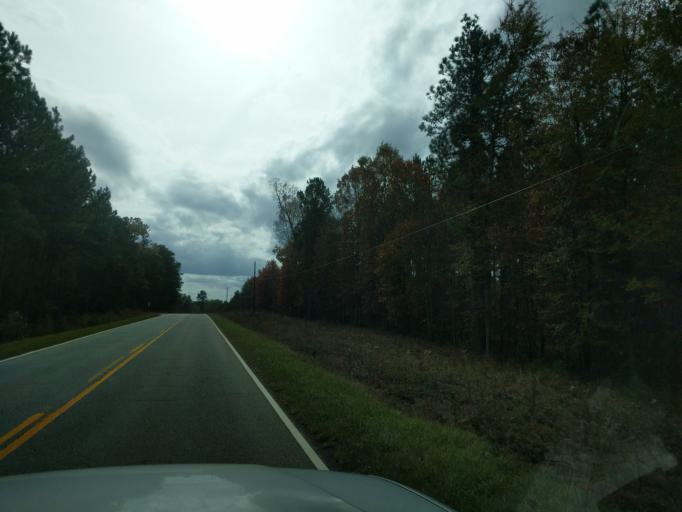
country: US
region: South Carolina
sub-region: Saluda County
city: Saluda
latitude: 34.0978
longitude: -81.8294
